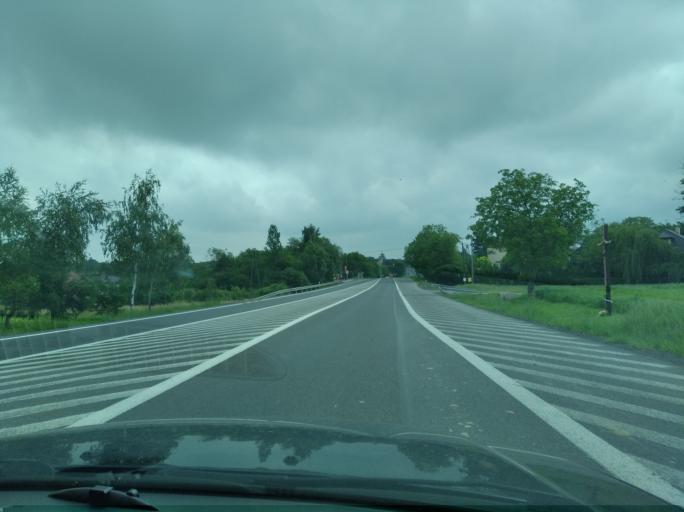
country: PL
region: Subcarpathian Voivodeship
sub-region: Powiat przeworski
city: Mirocin
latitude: 50.0447
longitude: 22.5476
